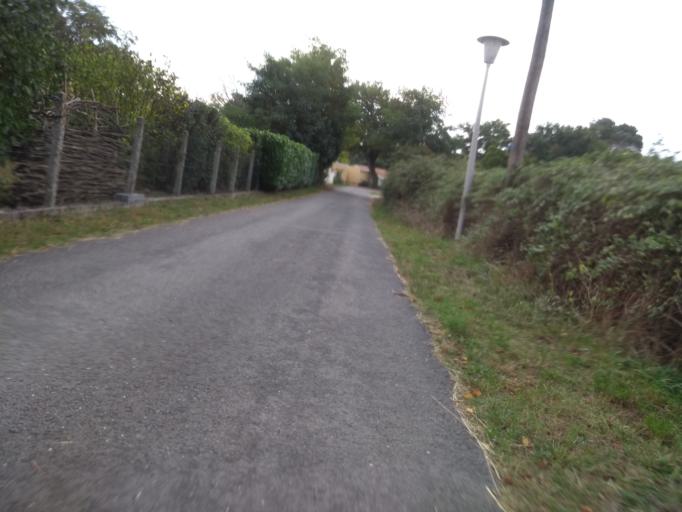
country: FR
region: Aquitaine
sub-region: Departement de la Gironde
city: Cestas
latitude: 44.7390
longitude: -0.6820
